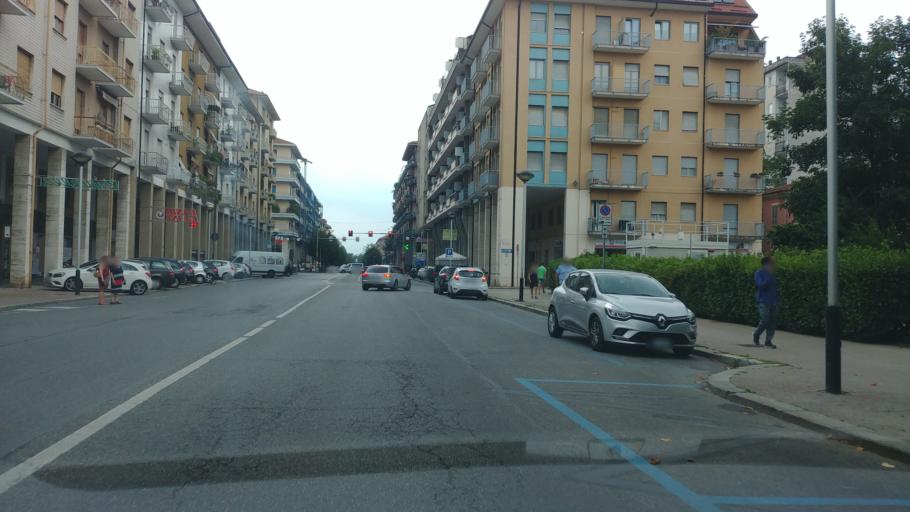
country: IT
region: Piedmont
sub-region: Provincia di Cuneo
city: Cuneo
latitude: 44.3821
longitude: 7.5379
